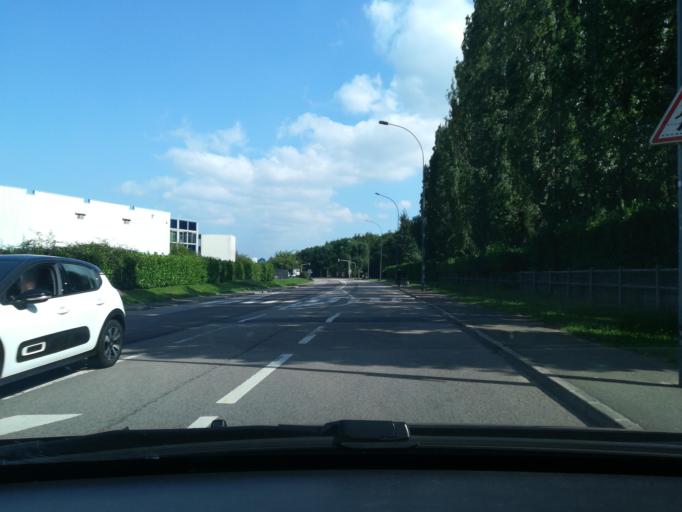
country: FR
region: Haute-Normandie
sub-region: Departement de la Seine-Maritime
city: Bois-Guillaume
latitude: 49.4626
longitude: 1.1197
